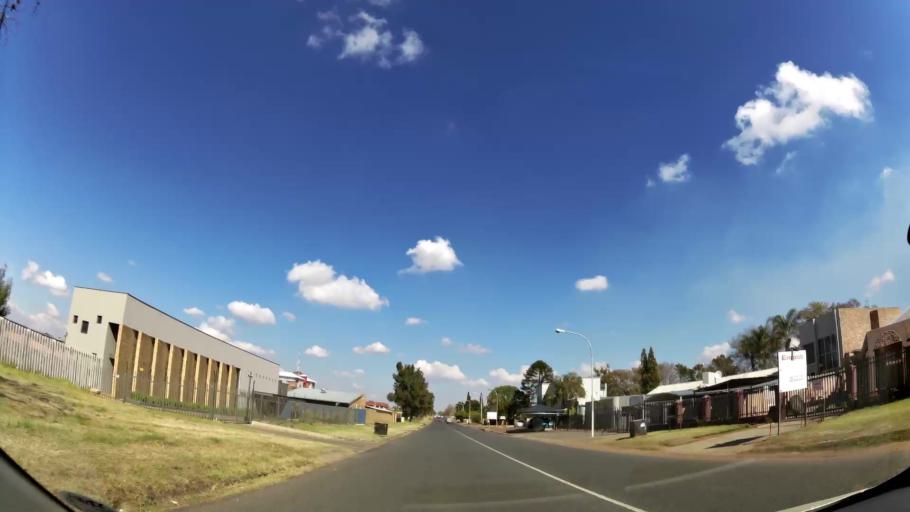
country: ZA
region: Mpumalanga
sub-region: Nkangala District Municipality
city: Witbank
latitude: -25.8809
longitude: 29.2310
